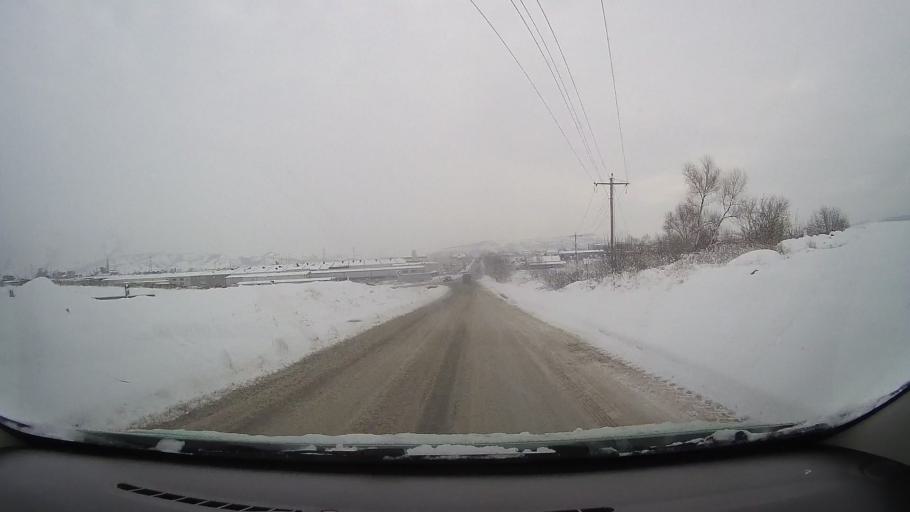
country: RO
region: Alba
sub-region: Municipiul Sebes
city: Lancram
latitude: 45.9599
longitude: 23.5374
